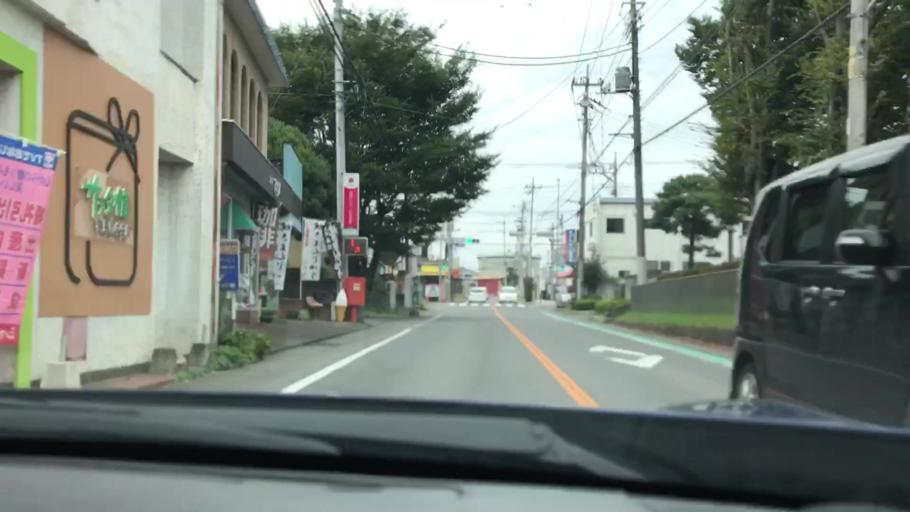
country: JP
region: Gunma
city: Kanekomachi
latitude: 36.3959
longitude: 138.9991
